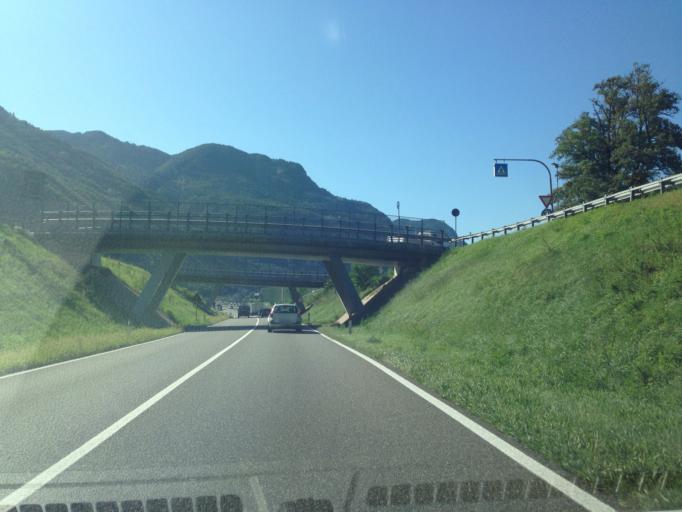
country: IT
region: Trentino-Alto Adige
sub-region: Bolzano
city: Pineta
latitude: 46.4435
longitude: 11.3431
